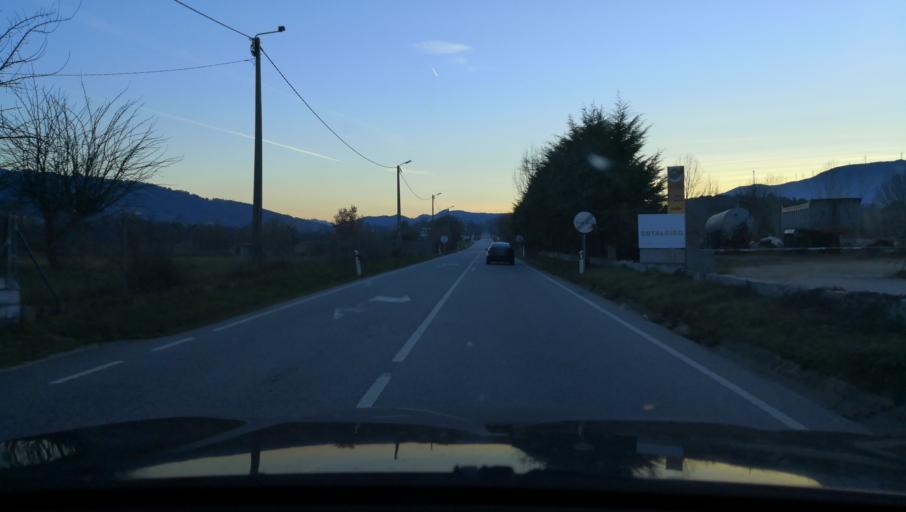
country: PT
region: Vila Real
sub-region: Vila Pouca de Aguiar
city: Vila Pouca de Aguiar
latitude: 41.4379
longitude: -7.6766
